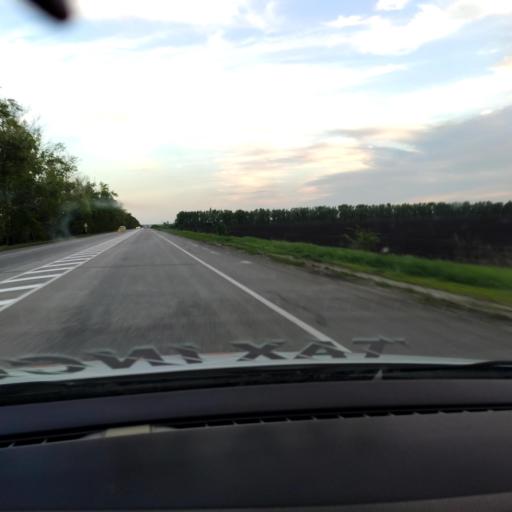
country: RU
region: Voronezj
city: Maslovka
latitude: 51.4432
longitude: 39.3026
